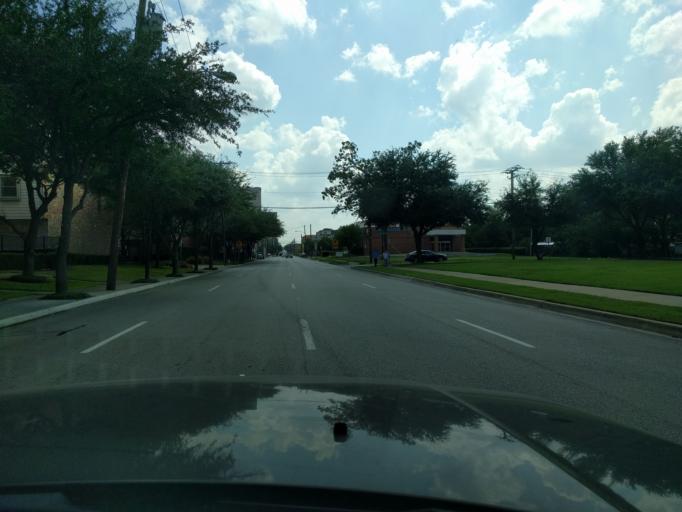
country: US
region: Texas
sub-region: Dallas County
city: Dallas
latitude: 32.8028
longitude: -96.7872
